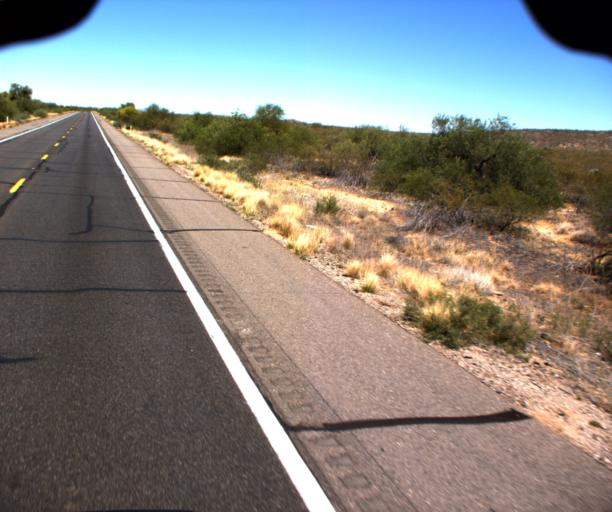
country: US
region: Arizona
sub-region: Yavapai County
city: Congress
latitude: 34.1698
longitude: -113.0173
